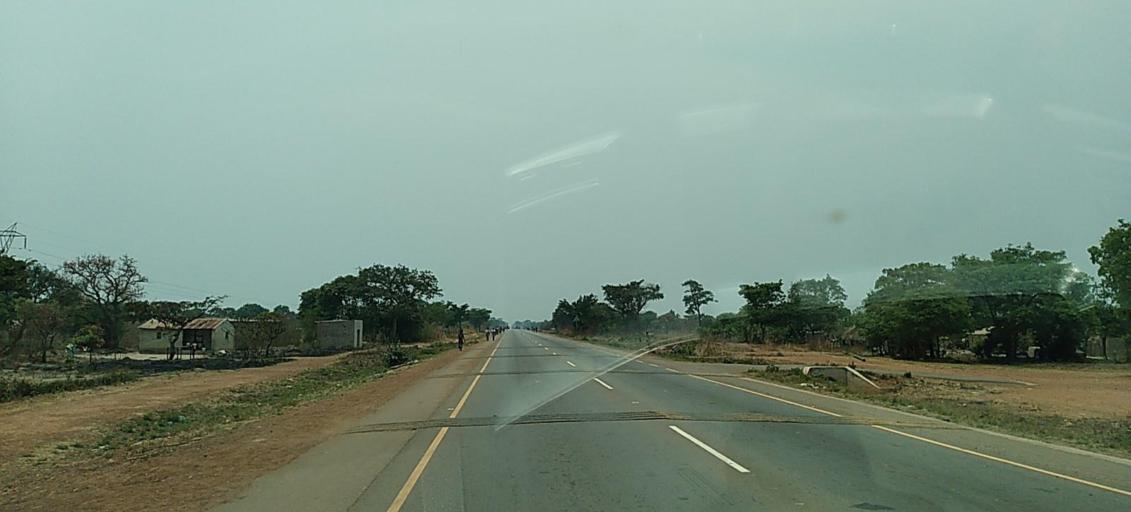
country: CD
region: Katanga
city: Kipushi
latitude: -12.3354
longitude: 27.0675
